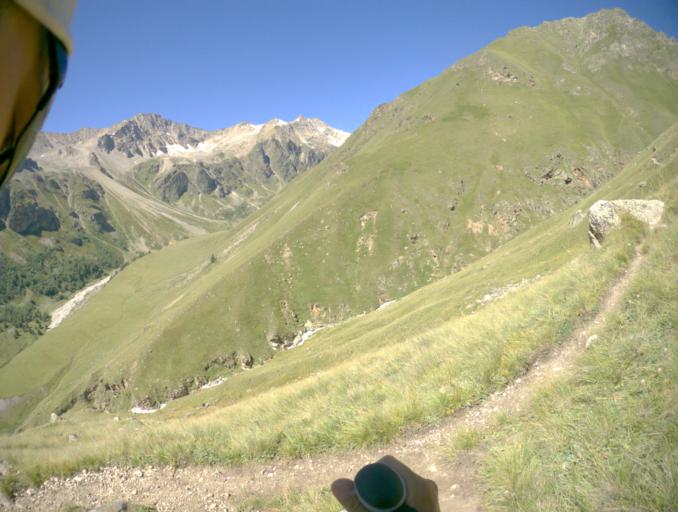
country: RU
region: Kabardino-Balkariya
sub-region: El'brusskiy Rayon
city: El'brus
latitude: 43.2981
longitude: 42.5883
